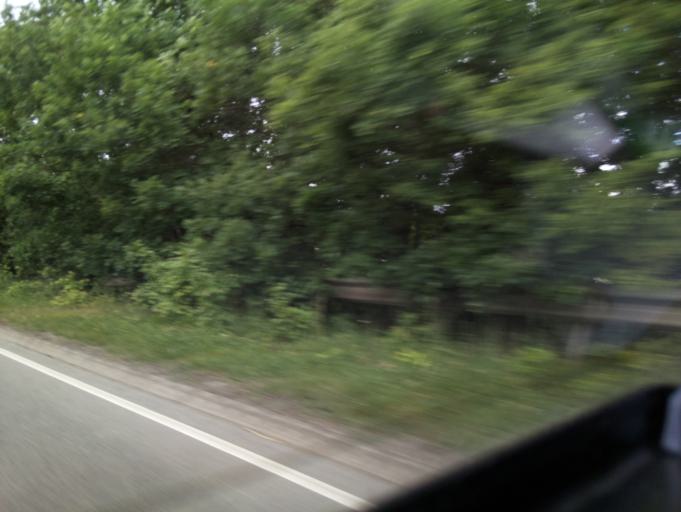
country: GB
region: England
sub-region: Warwickshire
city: Wellesbourne Mountford
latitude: 52.1334
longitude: -1.6140
